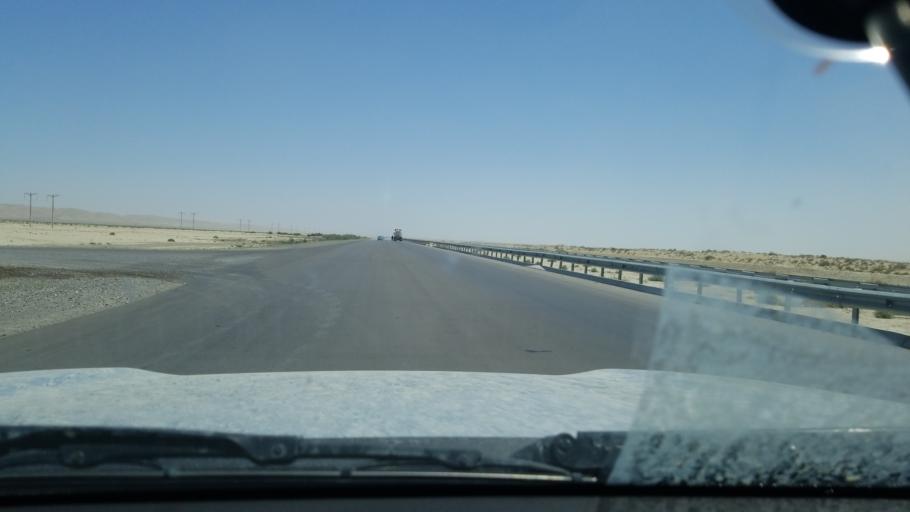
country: TM
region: Balkan
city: Gazanjyk
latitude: 39.2370
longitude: 55.0802
